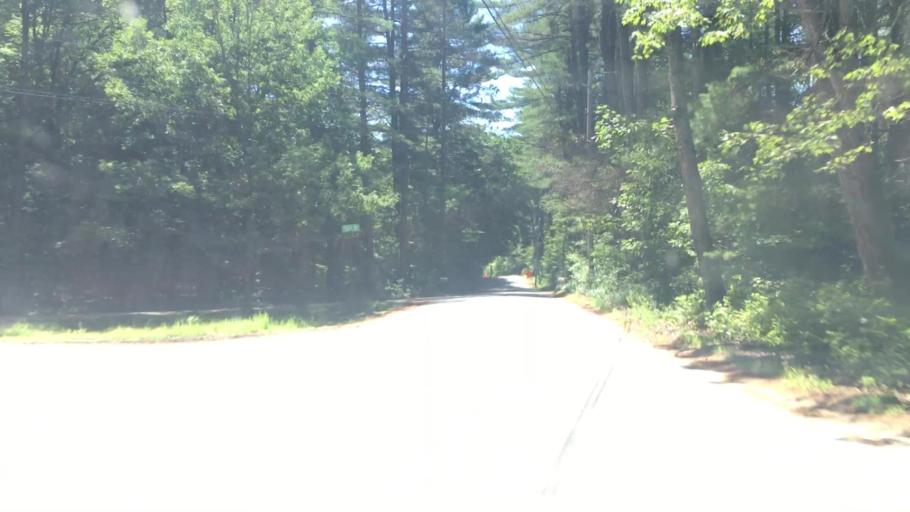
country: US
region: New Hampshire
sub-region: Merrimack County
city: Hopkinton
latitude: 43.2059
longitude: -71.6698
